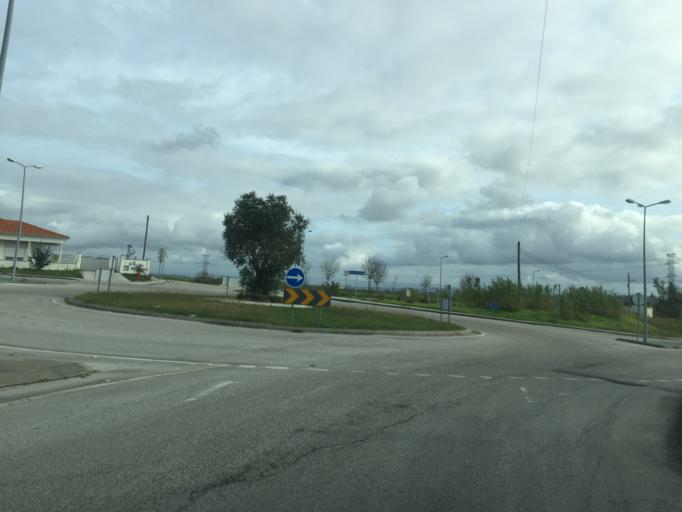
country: PT
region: Coimbra
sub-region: Figueira da Foz
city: Lavos
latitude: 40.0681
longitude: -8.8028
